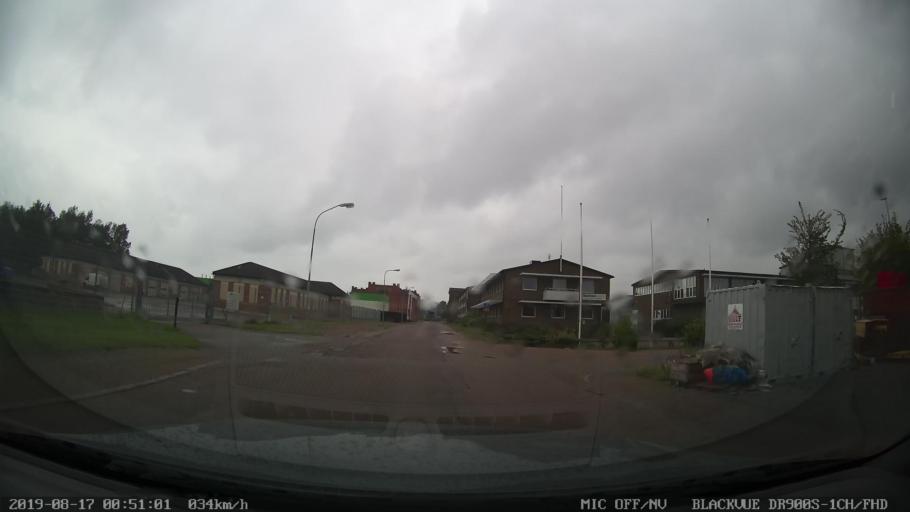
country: SE
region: Skane
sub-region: Landskrona
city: Landskrona
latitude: 55.8676
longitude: 12.8404
